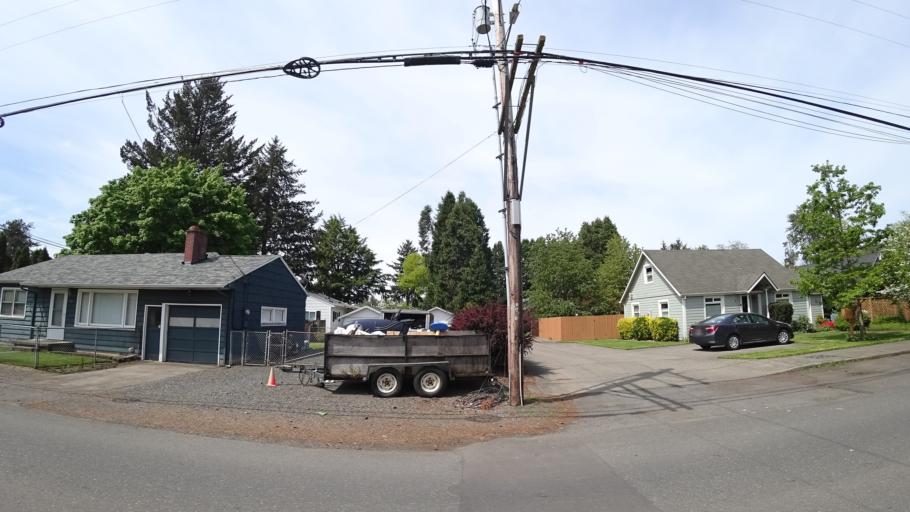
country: US
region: Oregon
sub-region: Clackamas County
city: Milwaukie
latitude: 45.4547
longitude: -122.6046
